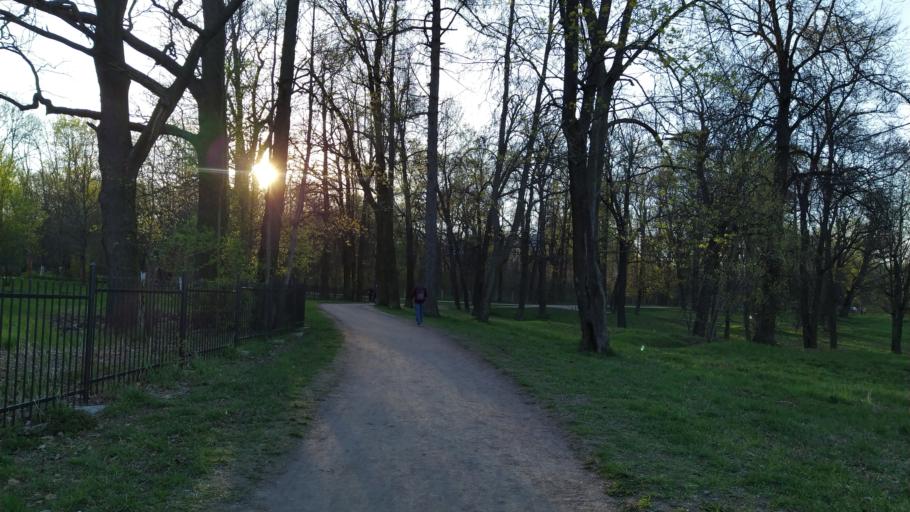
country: RU
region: St.-Petersburg
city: Pushkin
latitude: 59.7070
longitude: 30.4208
